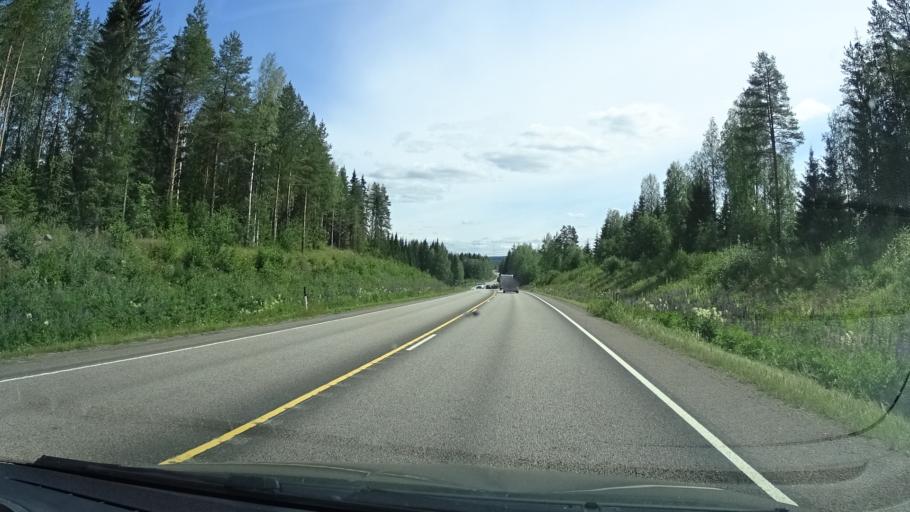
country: FI
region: Central Finland
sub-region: Jyvaeskylae
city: Uurainen
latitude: 62.2669
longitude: 25.4342
